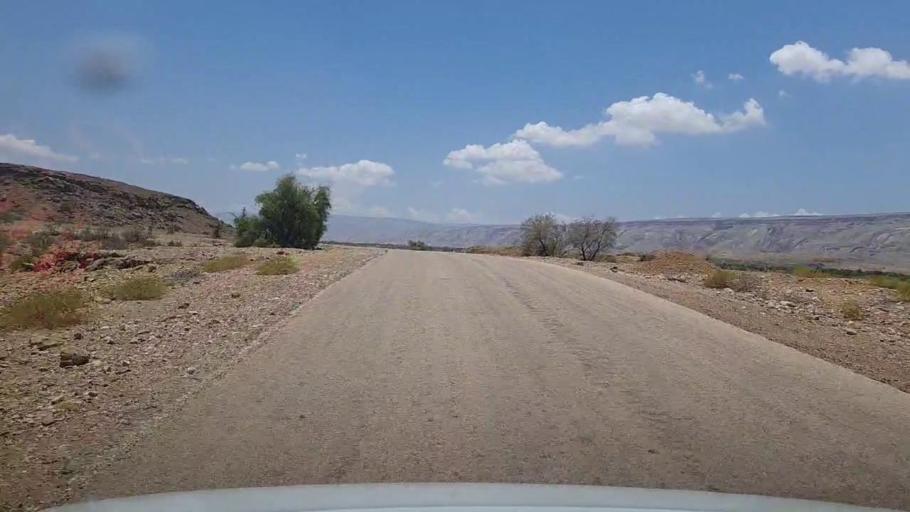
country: PK
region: Sindh
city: Bhan
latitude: 26.3092
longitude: 67.5377
